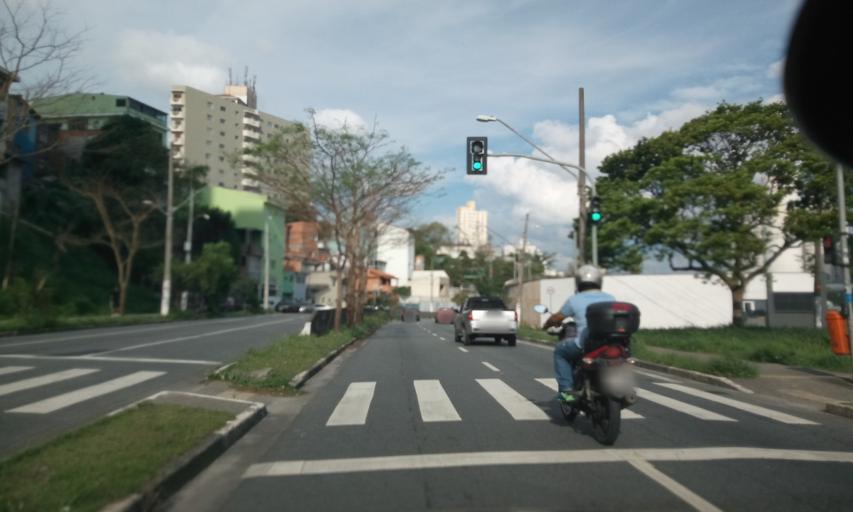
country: BR
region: Sao Paulo
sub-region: Sao Bernardo Do Campo
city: Sao Bernardo do Campo
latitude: -23.7001
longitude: -46.5489
